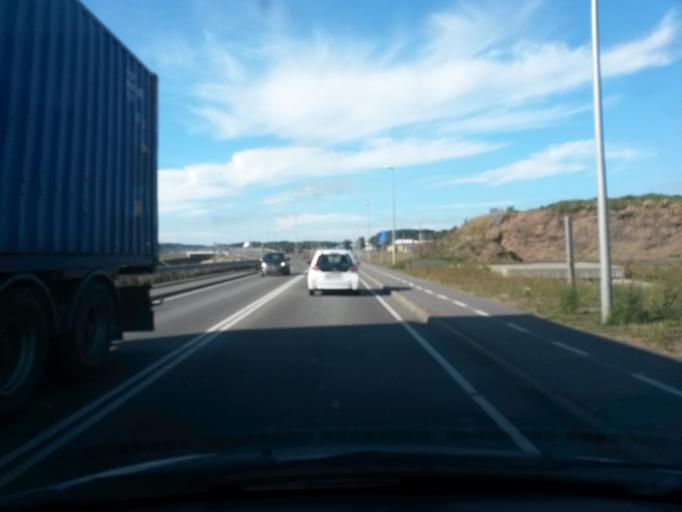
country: DK
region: Central Jutland
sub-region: Silkeborg Kommune
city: Silkeborg
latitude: 56.1840
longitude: 9.5819
